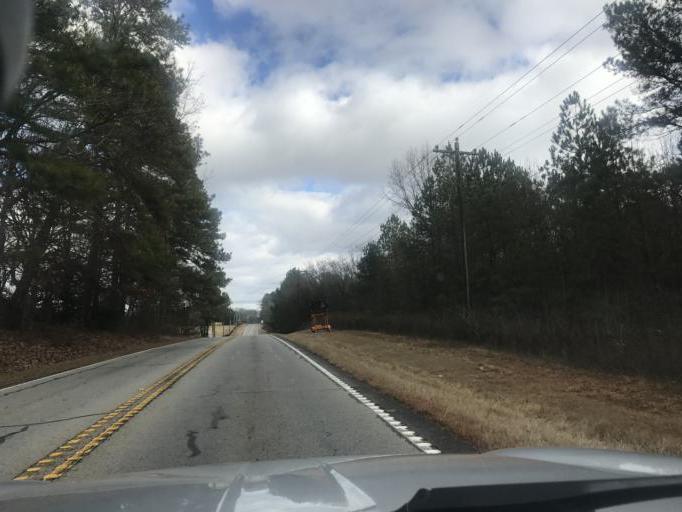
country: US
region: Georgia
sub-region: Barrow County
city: Russell
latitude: 34.0261
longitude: -83.6746
